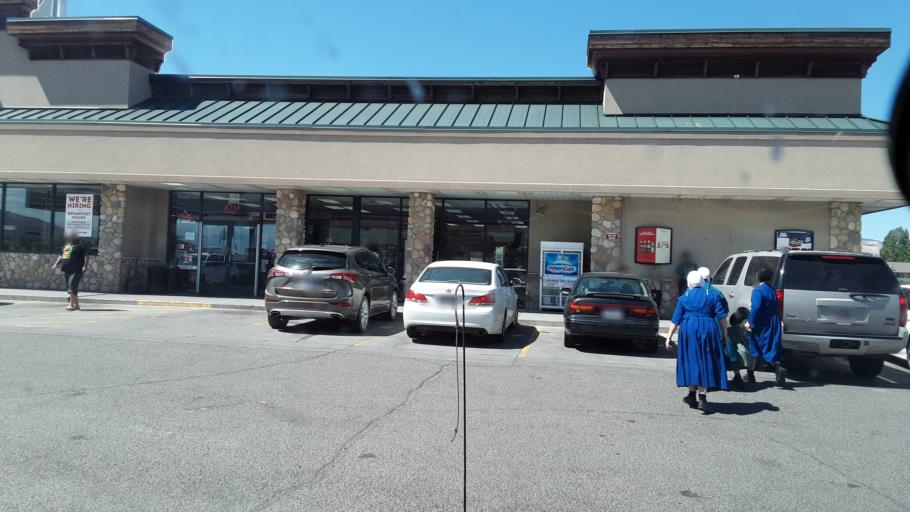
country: US
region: Utah
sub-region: Sevier County
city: Richfield
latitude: 38.7508
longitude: -112.1025
